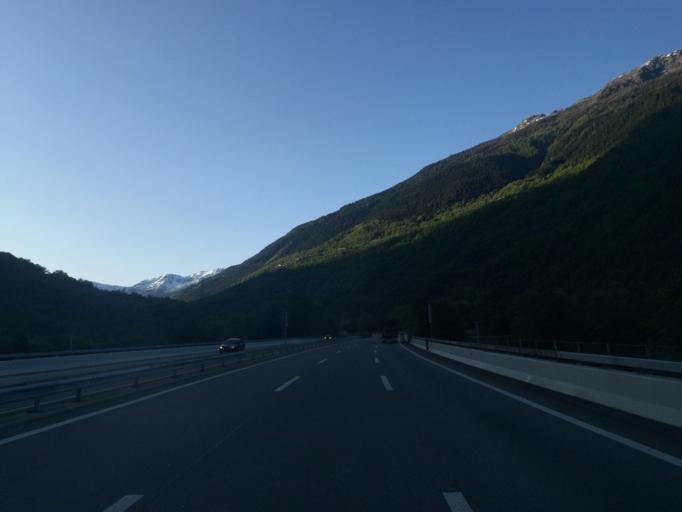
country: CH
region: Ticino
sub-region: Leventina District
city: Bodio
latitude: 46.4044
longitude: 8.8664
